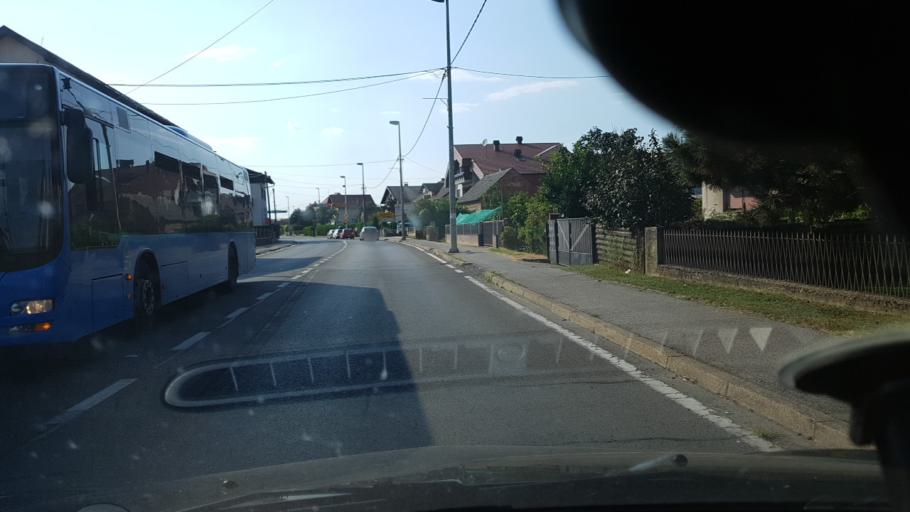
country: HR
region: Zagrebacka
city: Zapresic
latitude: 45.8604
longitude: 15.7984
